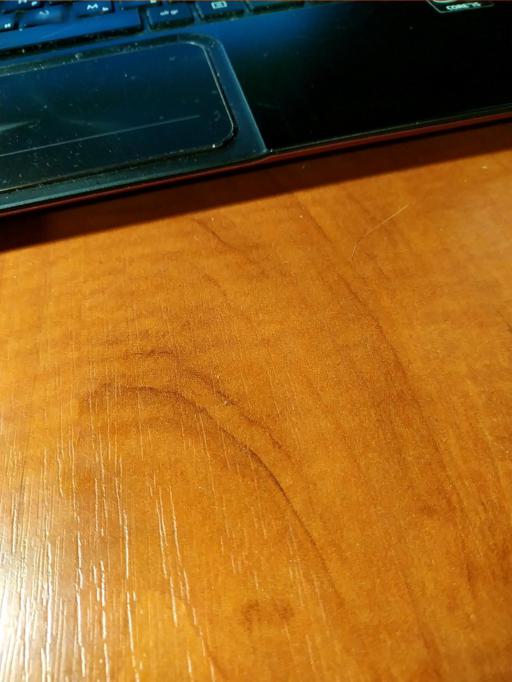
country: RU
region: Smolensk
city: Ozernyy
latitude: 55.4349
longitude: 32.7113
